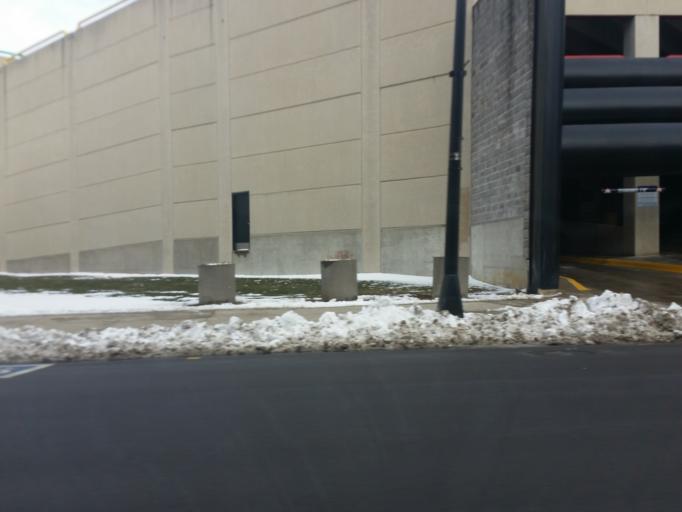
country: US
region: Iowa
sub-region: Black Hawk County
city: Waterloo
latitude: 42.4949
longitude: -92.3394
